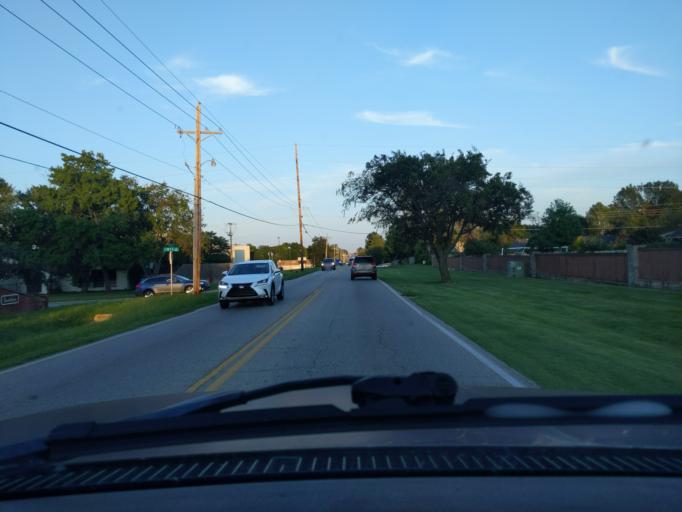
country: US
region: Oklahoma
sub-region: Tulsa County
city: Jenks
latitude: 36.0464
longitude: -95.8963
